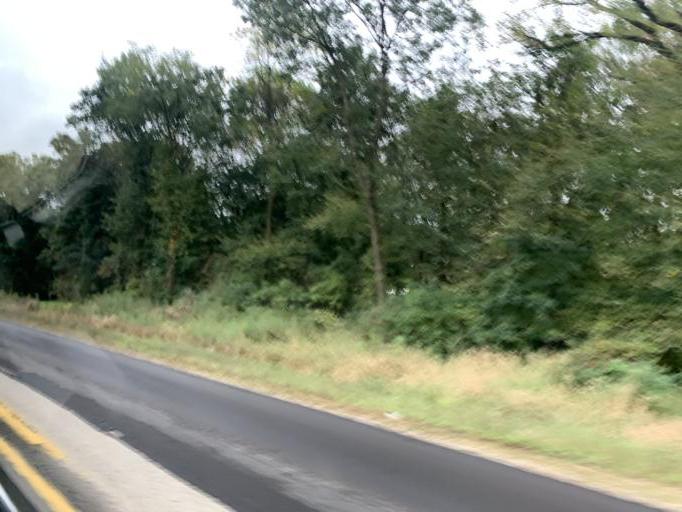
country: US
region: Wisconsin
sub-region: Grant County
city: Muscoda
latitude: 43.2052
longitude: -90.4037
